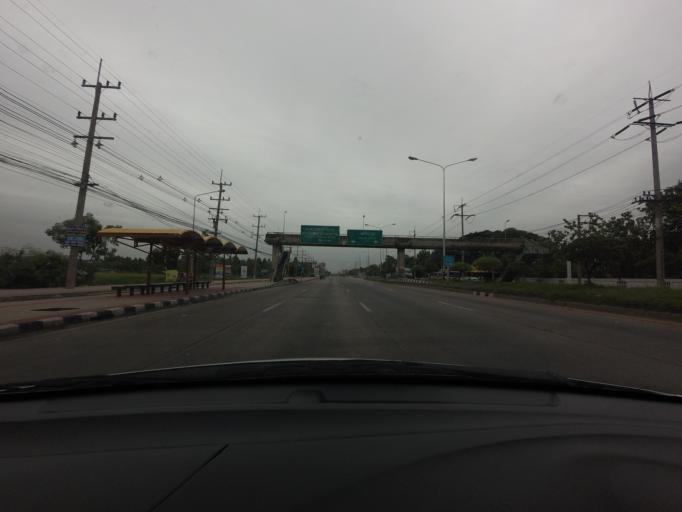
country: TH
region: Nakhon Pathom
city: Sam Phran
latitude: 13.7181
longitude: 100.2589
